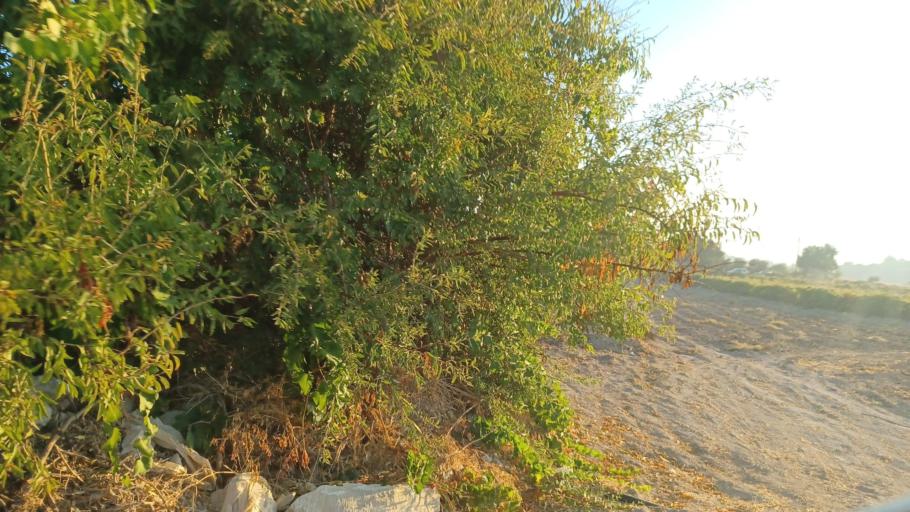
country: CY
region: Pafos
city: Mesogi
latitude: 34.8458
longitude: 32.5146
